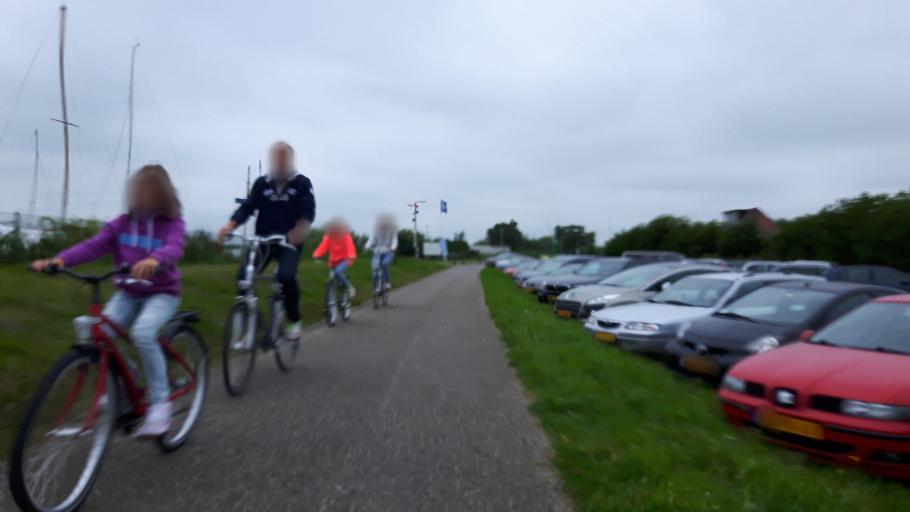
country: NL
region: South Holland
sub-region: Gemeente Kaag en Braassem
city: Oude Wetering
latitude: 52.1959
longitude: 4.6404
